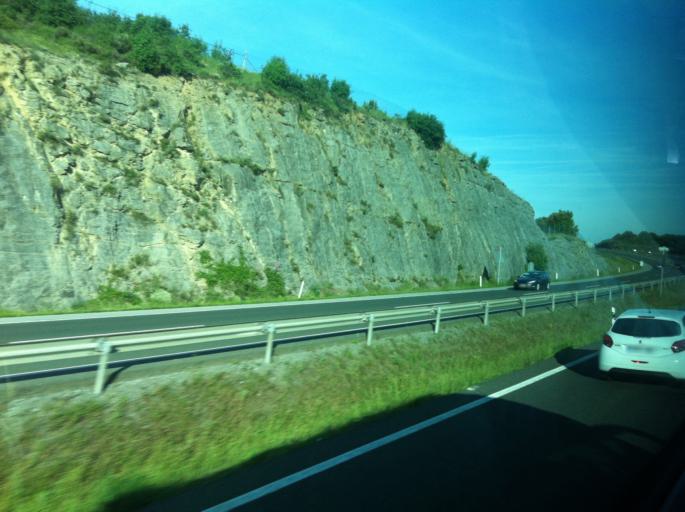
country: ES
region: Basque Country
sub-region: Provincia de Alava
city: Murguia
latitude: 42.9326
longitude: -2.7442
